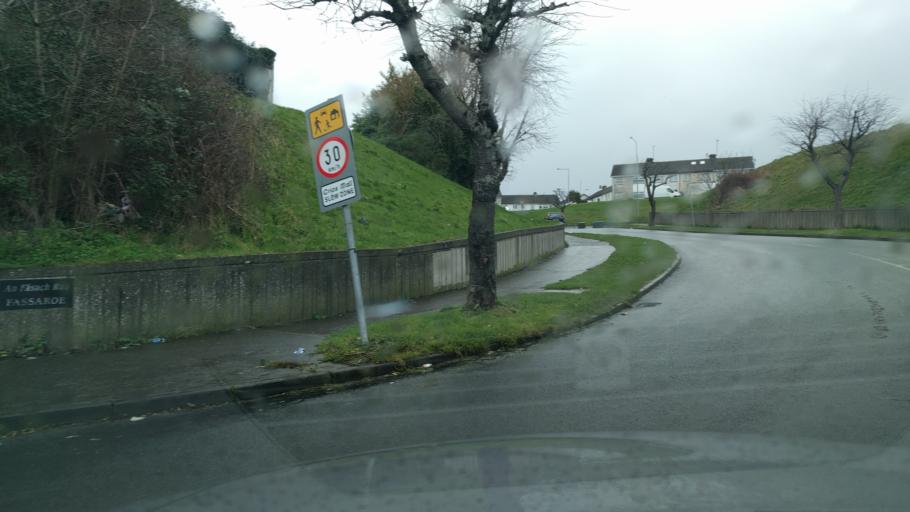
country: IE
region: Leinster
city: Little Bray
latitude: 53.2038
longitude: -6.1215
